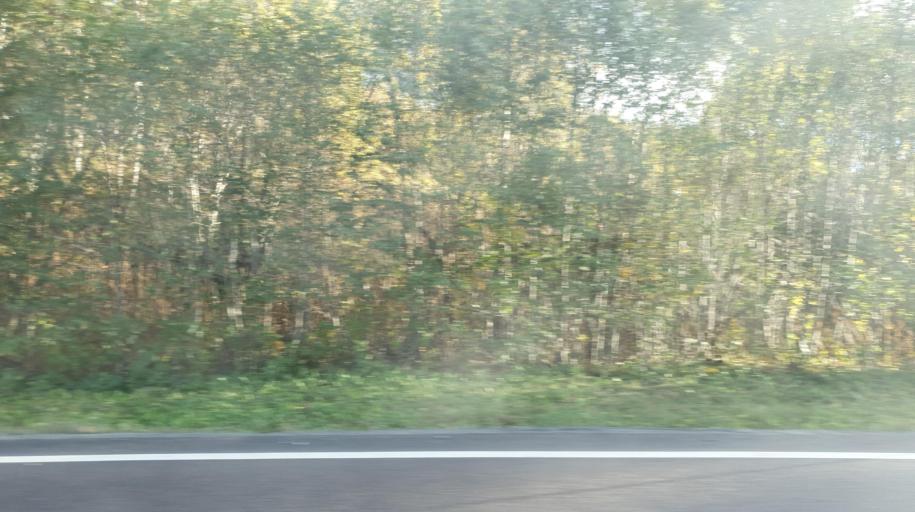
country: NO
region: Sor-Trondelag
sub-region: Klaebu
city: Klaebu
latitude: 63.3082
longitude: 10.4579
